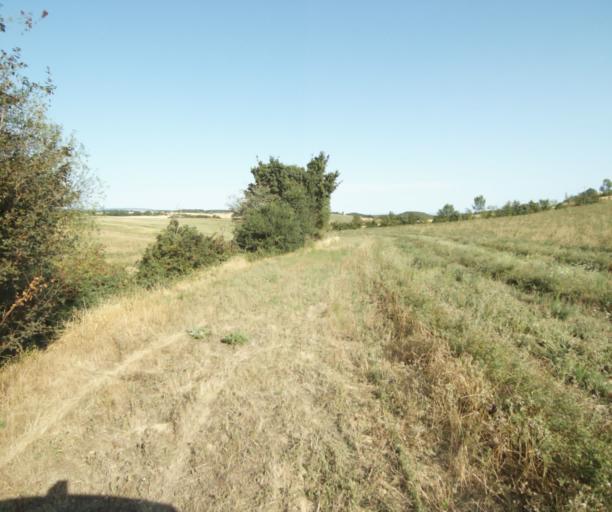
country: FR
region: Midi-Pyrenees
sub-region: Departement de la Haute-Garonne
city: Avignonet-Lauragais
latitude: 43.4271
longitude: 1.8190
